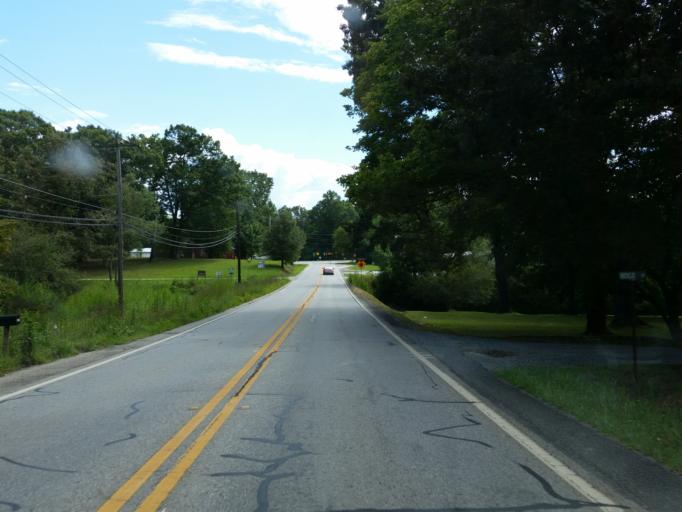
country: US
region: Georgia
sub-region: Fannin County
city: Blue Ridge
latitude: 34.8881
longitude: -84.2615
